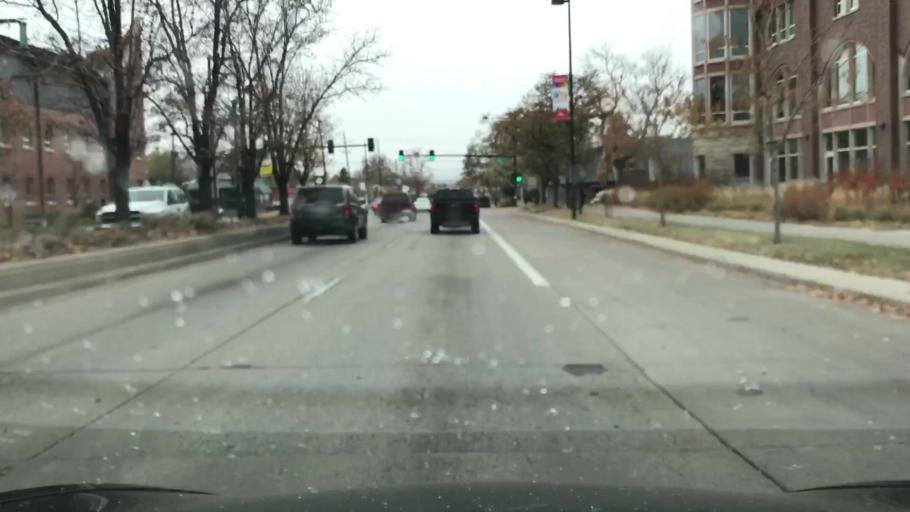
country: US
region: Colorado
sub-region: Arapahoe County
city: Cherry Hills Village
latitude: 39.6785
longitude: -104.9642
